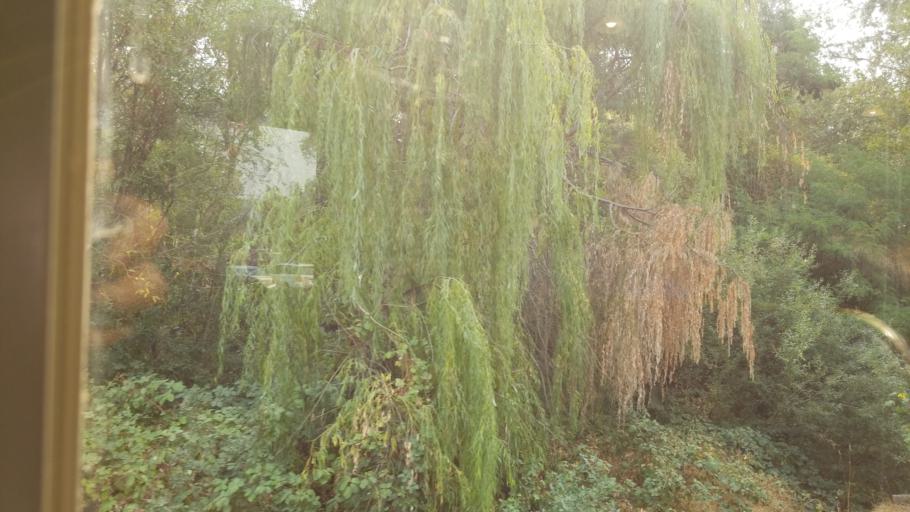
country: US
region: California
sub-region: Mendocino County
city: Willits
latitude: 39.4104
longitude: -123.3506
